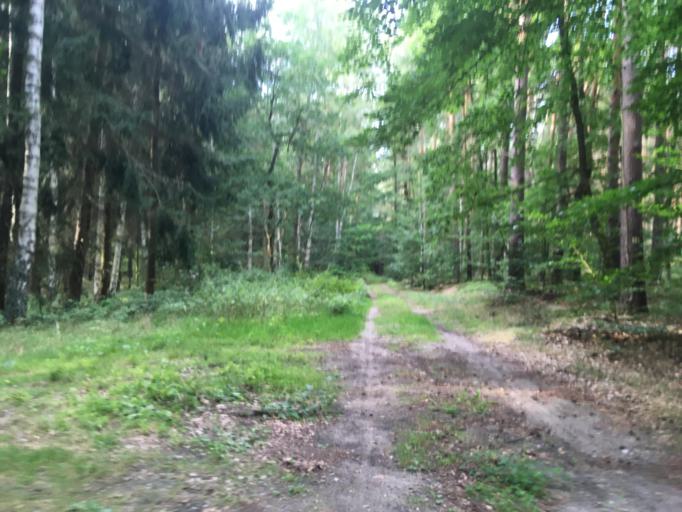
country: DE
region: Brandenburg
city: Eberswalde
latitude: 52.7968
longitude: 13.8203
